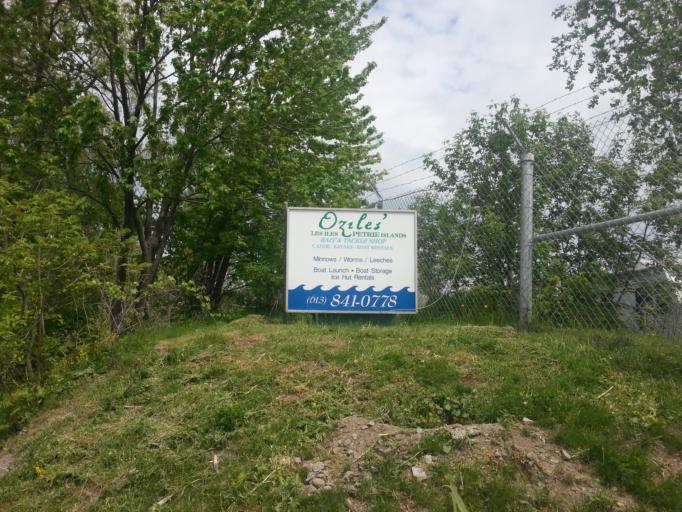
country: CA
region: Ontario
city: Clarence-Rockland
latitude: 45.5005
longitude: -75.4850
